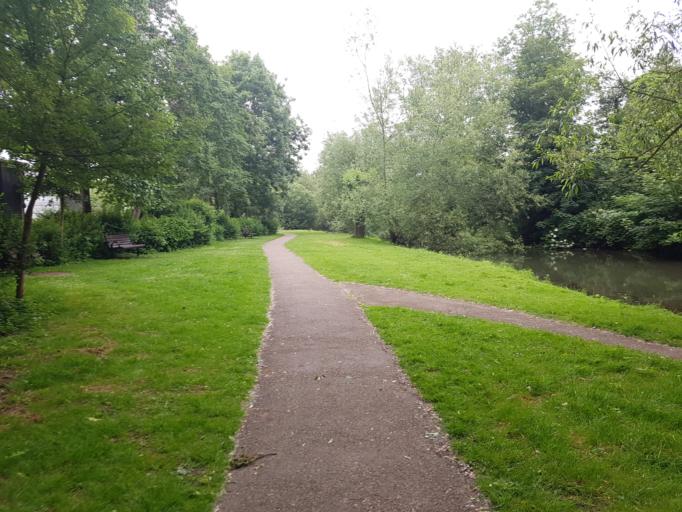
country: GB
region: England
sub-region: Buckinghamshire
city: Buckingham
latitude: 51.9996
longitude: -0.9843
